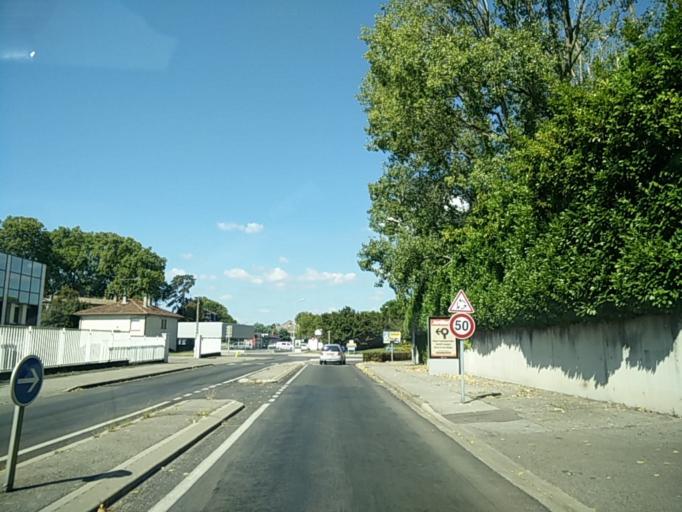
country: FR
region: Rhone-Alpes
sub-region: Departement de la Drome
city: Montelimar
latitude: 44.5501
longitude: 4.7756
